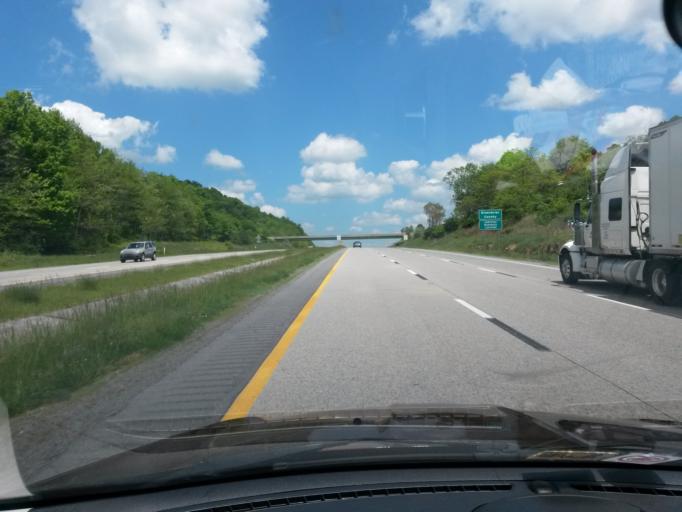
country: US
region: West Virginia
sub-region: Greenbrier County
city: Rainelle
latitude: 37.8388
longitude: -80.7567
